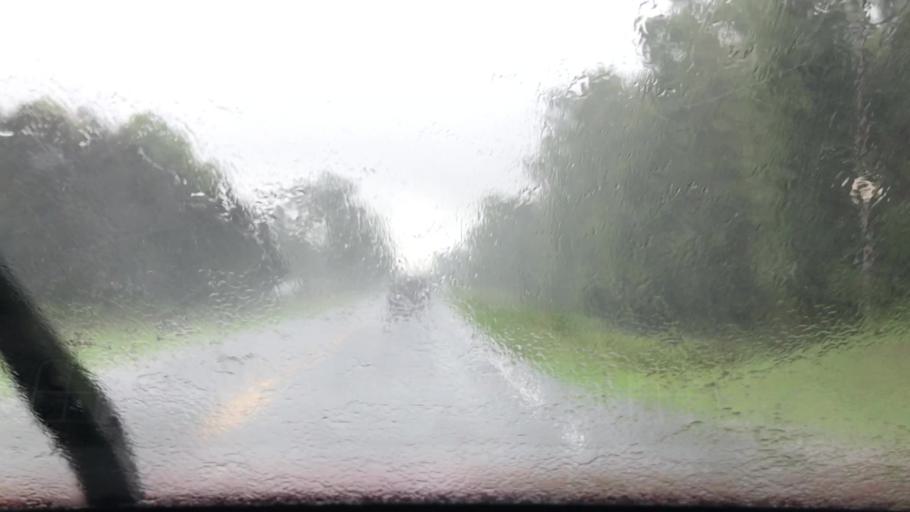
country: US
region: South Carolina
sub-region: Horry County
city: Red Hill
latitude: 33.9030
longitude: -78.9019
